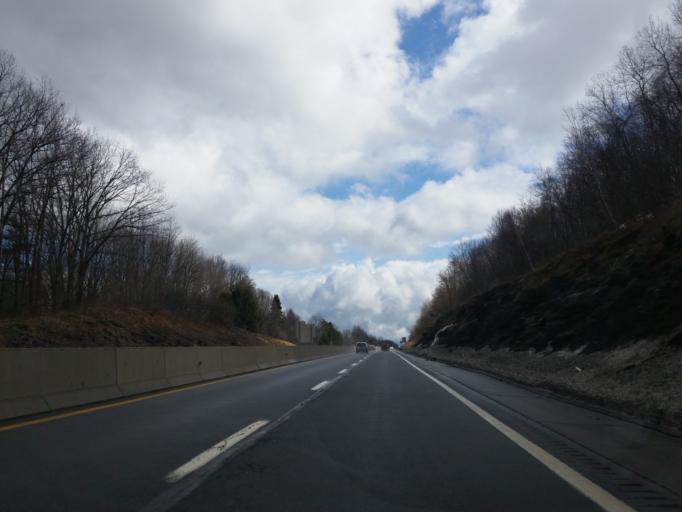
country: US
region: Pennsylvania
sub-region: Lackawanna County
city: Clarks Summit
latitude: 41.4664
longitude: -75.7001
